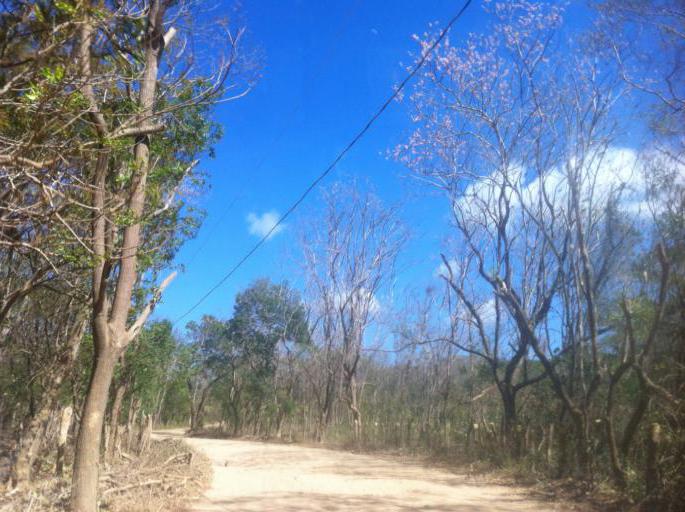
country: NI
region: Rivas
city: Tola
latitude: 11.3866
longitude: -86.0149
